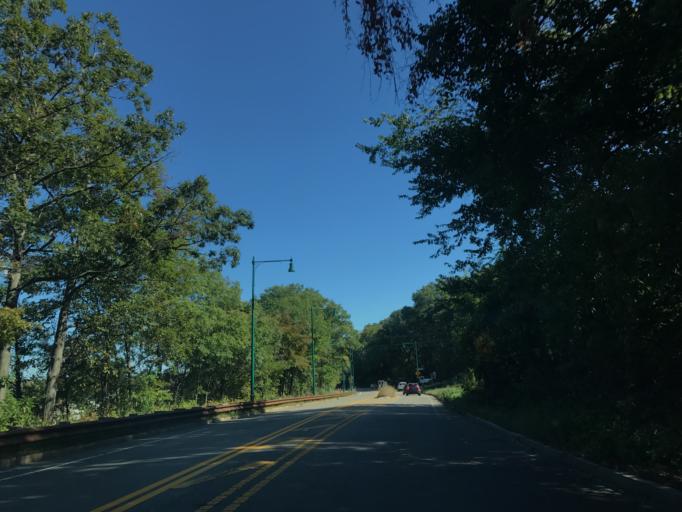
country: US
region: Massachusetts
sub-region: Middlesex County
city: Watertown
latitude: 42.3587
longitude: -71.1764
